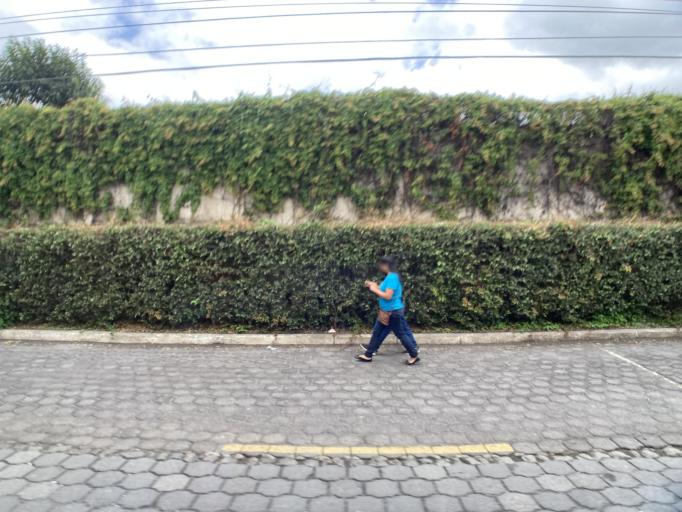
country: GT
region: Sacatepequez
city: Jocotenango
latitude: 14.5753
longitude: -90.7453
